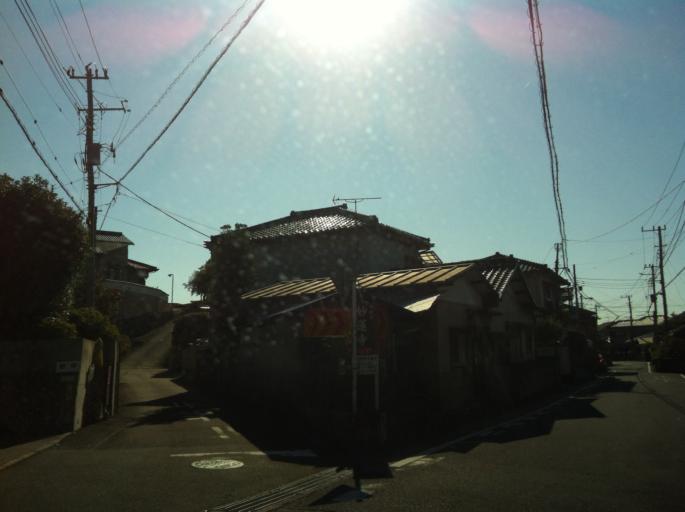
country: JP
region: Shizuoka
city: Fuji
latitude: 35.1608
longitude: 138.7461
